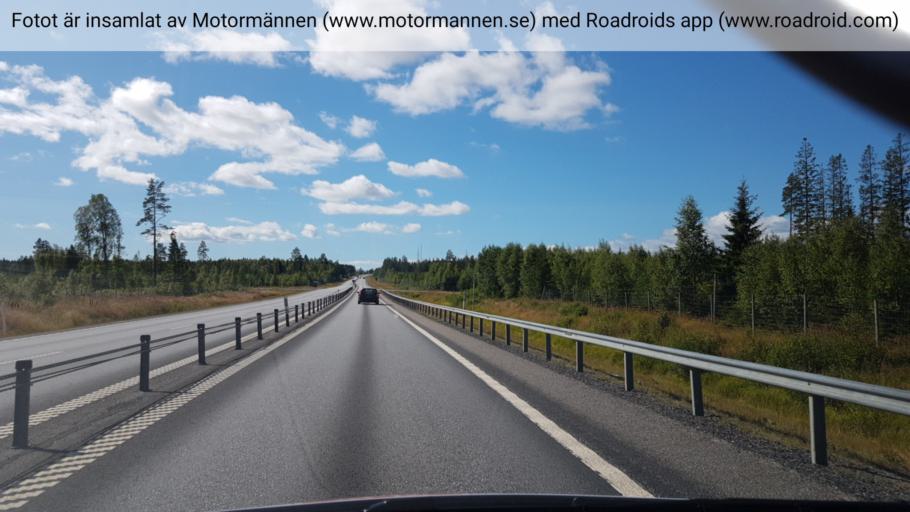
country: SE
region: Vaesterbotten
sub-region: Umea Kommun
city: Hoernefors
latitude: 63.6652
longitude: 19.9679
